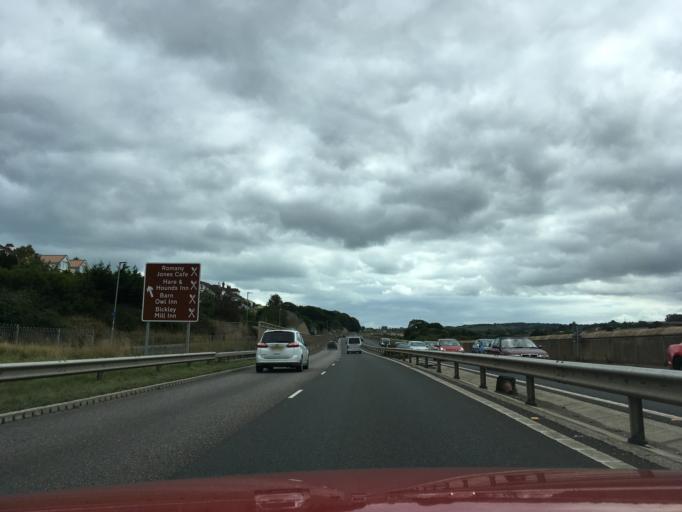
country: GB
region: England
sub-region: Devon
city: Newton Abbot
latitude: 50.5198
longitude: -3.5915
